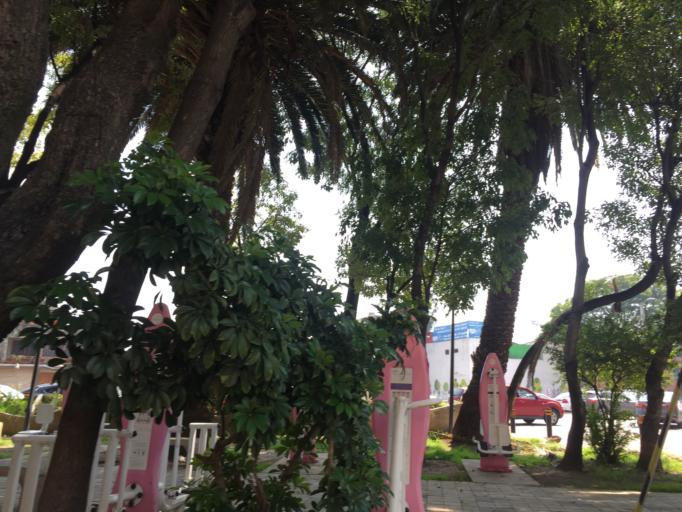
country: MX
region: Mexico
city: Colonia Lindavista
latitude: 19.4787
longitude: -99.1218
